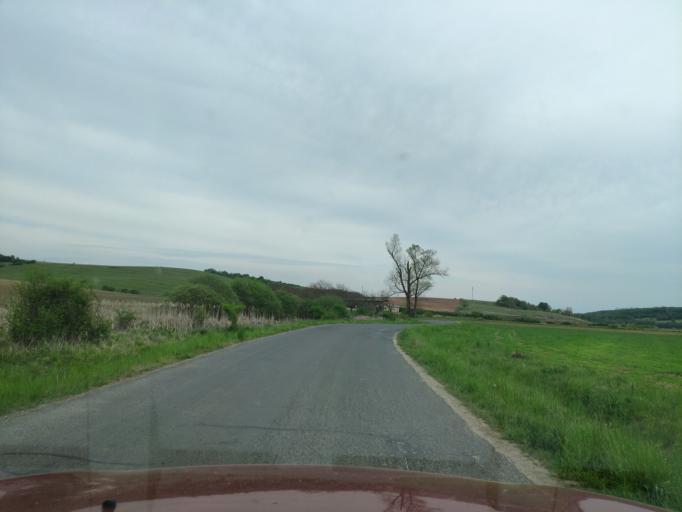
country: SK
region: Banskobystricky
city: Revuca
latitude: 48.4959
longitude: 20.2169
